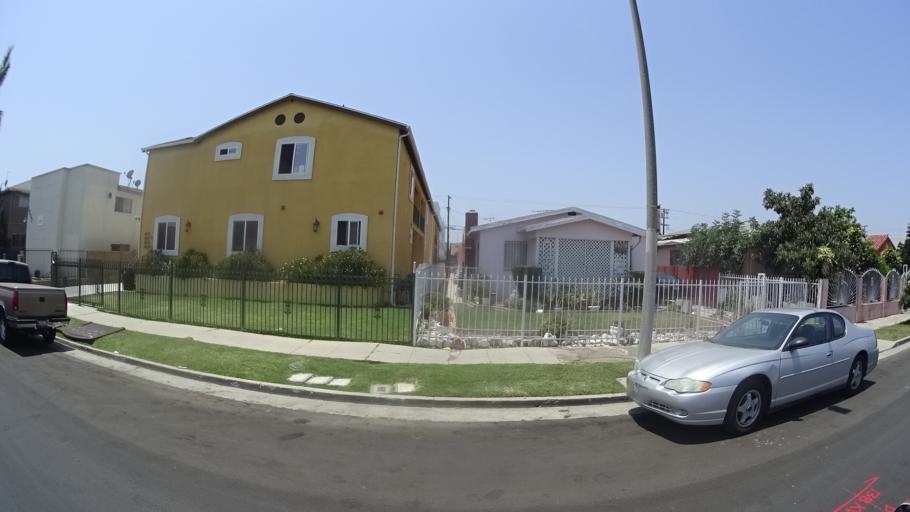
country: US
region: California
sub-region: Los Angeles County
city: View Park-Windsor Hills
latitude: 33.9792
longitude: -118.3340
